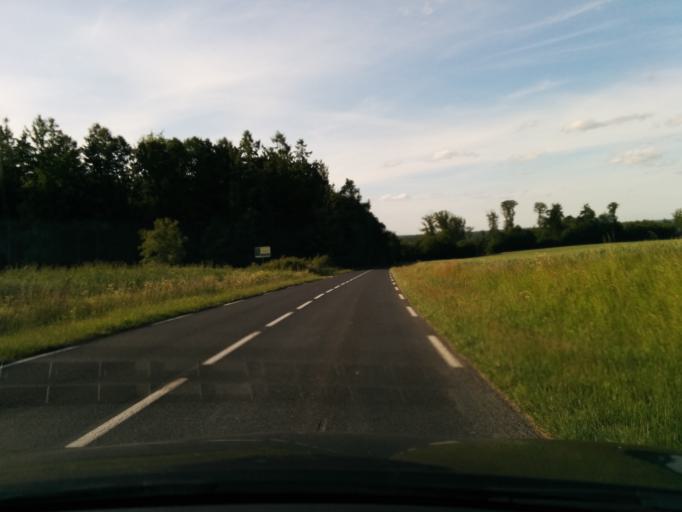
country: FR
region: Haute-Normandie
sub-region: Departement de l'Eure
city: Charleval
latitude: 49.3879
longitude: 1.4695
